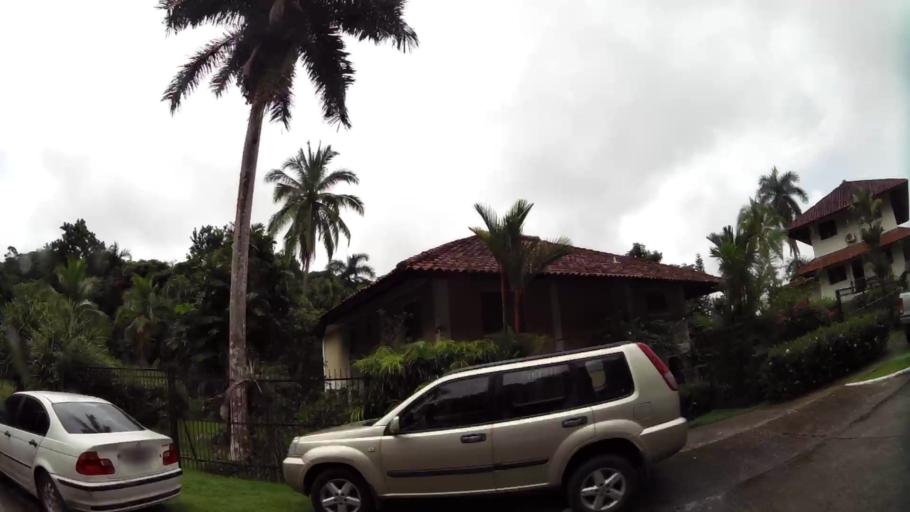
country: PA
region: Panama
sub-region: Distrito de Panama
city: Ancon
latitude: 8.9821
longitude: -79.5657
